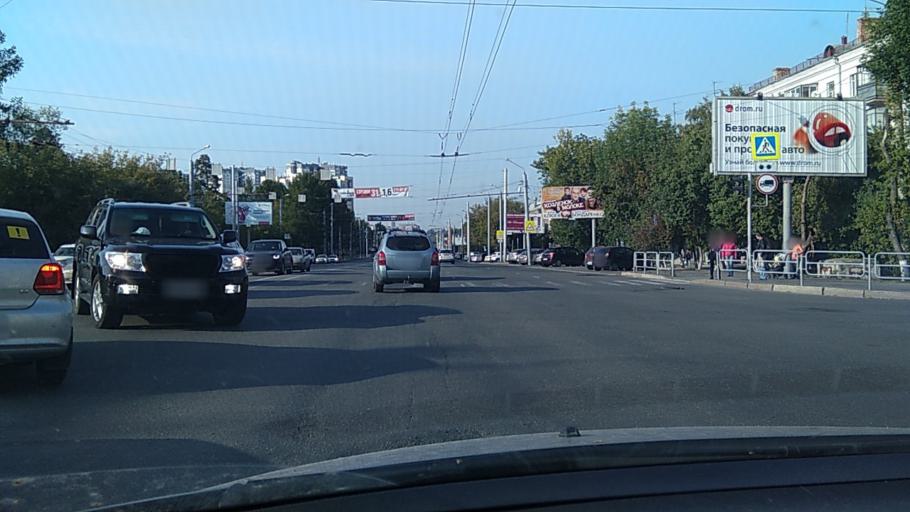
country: RU
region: Chelyabinsk
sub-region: Gorod Chelyabinsk
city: Chelyabinsk
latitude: 55.1622
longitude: 61.3812
